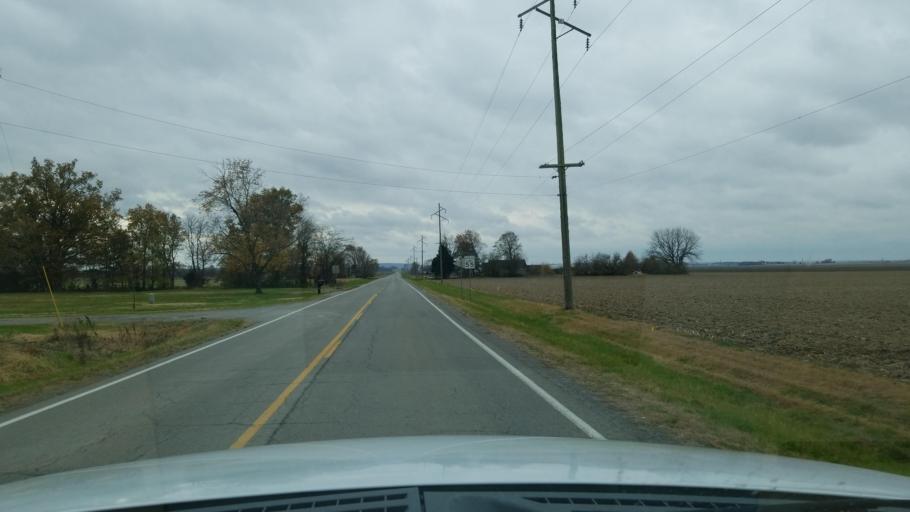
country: US
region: Illinois
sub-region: Saline County
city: Eldorado
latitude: 37.7901
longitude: -88.4382
